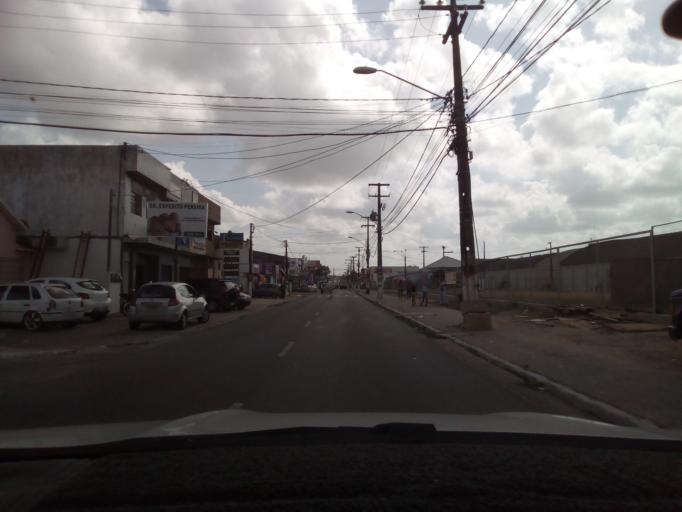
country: BR
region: Paraiba
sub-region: Bayeux
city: Bayeux
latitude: -7.1242
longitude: -34.9216
